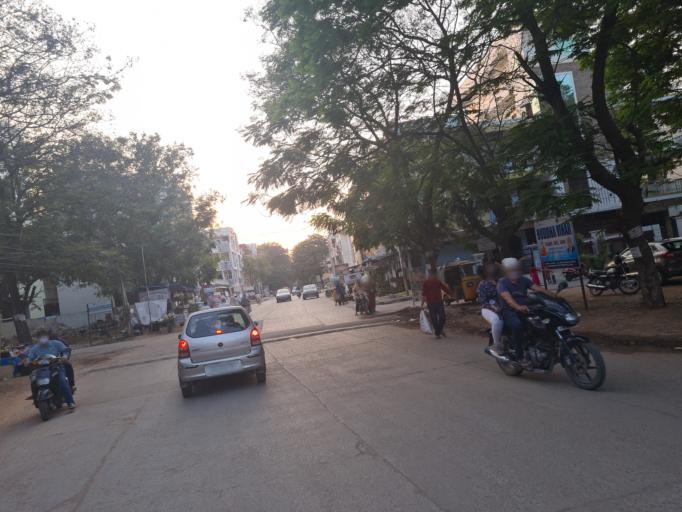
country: IN
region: Telangana
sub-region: Medak
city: Serilingampalle
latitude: 17.4780
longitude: 78.2904
